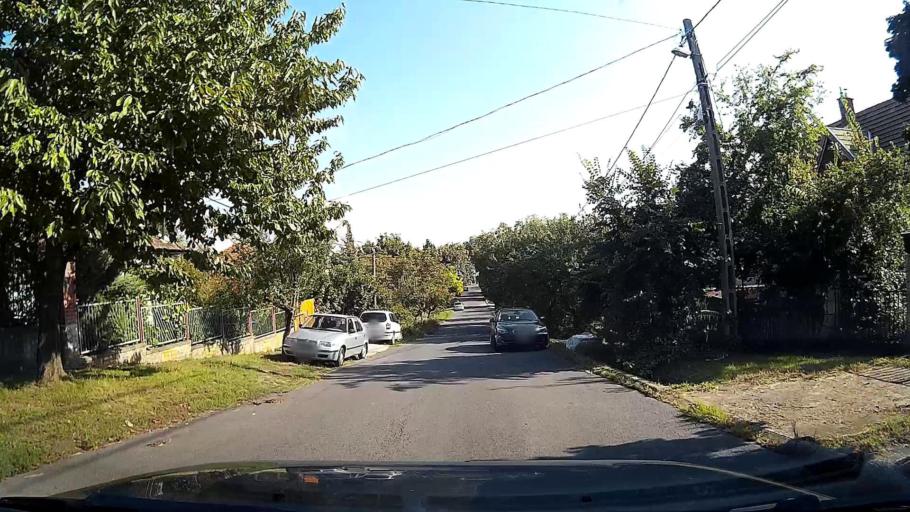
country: HU
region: Budapest
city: Budapest XXII. keruelet
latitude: 47.4127
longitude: 19.0225
